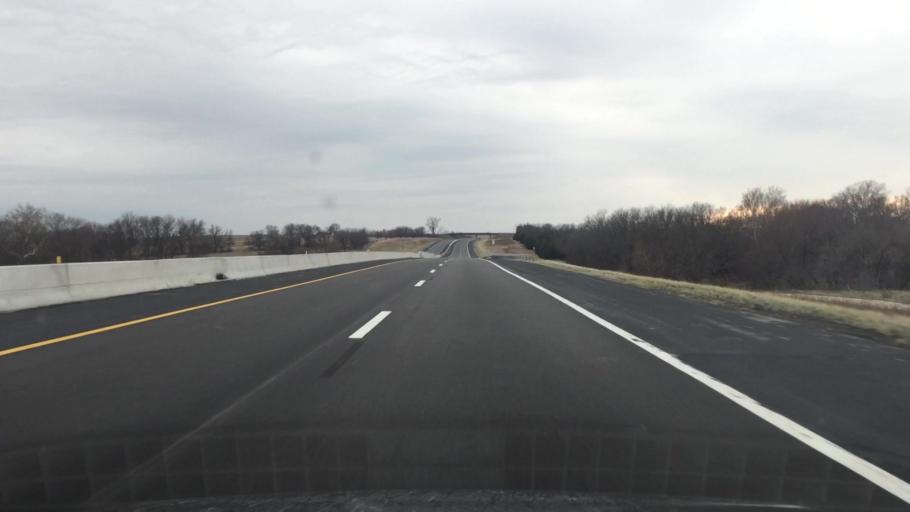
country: US
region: Kansas
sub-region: Osage County
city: Osage City
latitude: 38.7731
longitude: -95.9236
